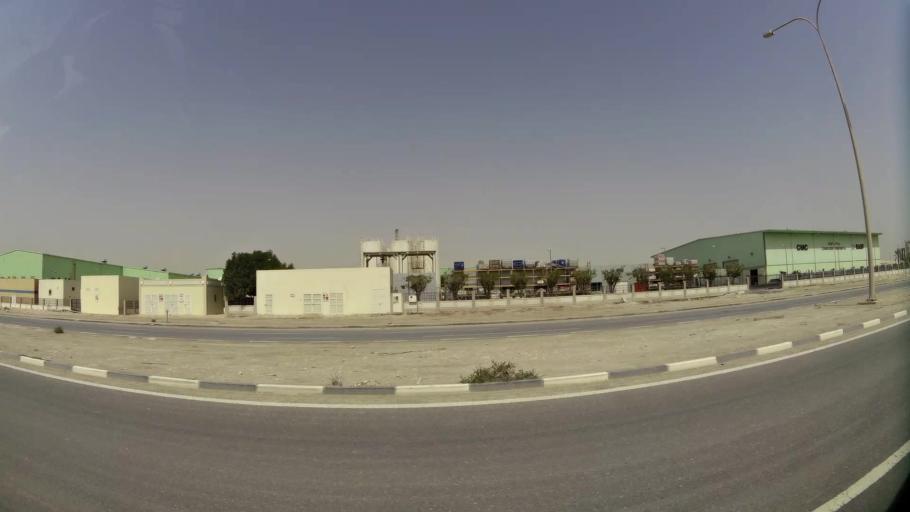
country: QA
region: Al Wakrah
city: Al Wukayr
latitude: 25.1614
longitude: 51.4122
